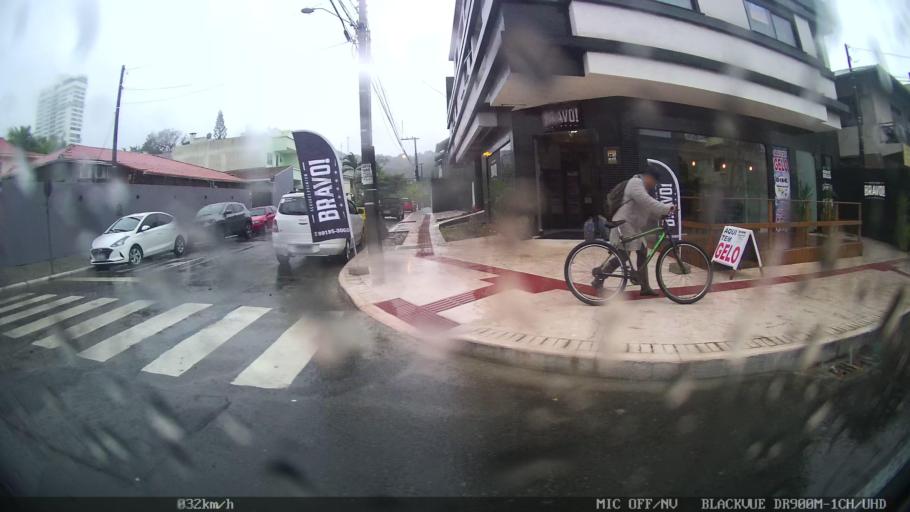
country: BR
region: Santa Catarina
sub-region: Balneario Camboriu
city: Balneario Camboriu
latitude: -26.9557
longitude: -48.6360
